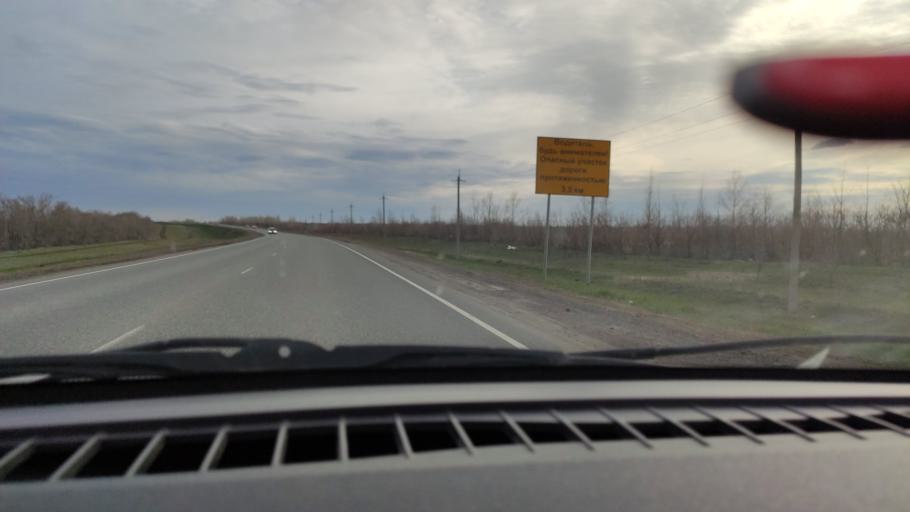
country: RU
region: Orenburg
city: Tatarskaya Kargala
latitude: 52.0150
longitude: 55.2065
